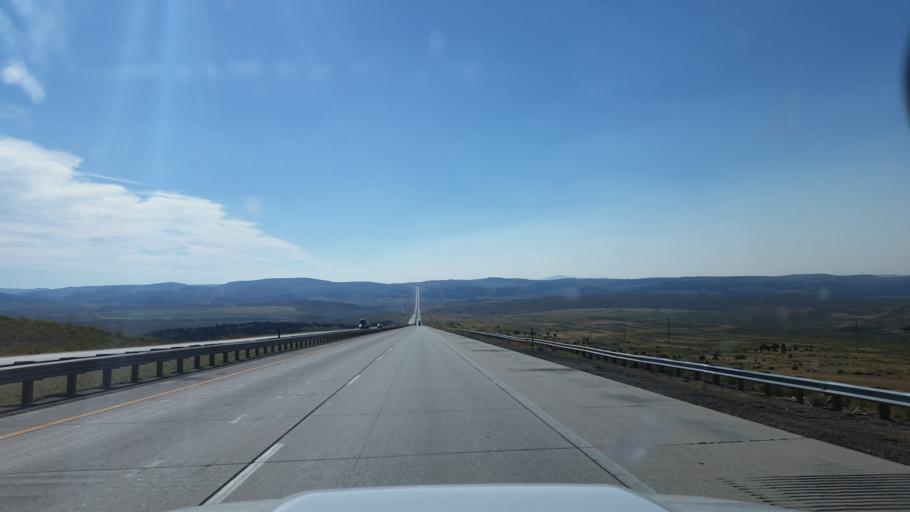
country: US
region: Wyoming
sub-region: Uinta County
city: Mountain View
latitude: 41.2975
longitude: -110.5649
